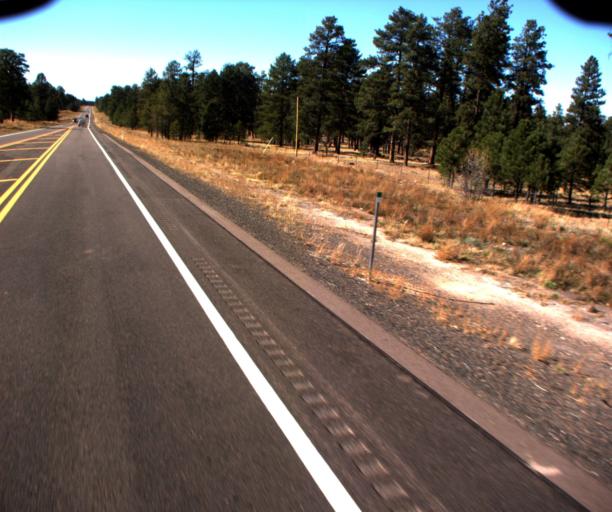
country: US
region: Arizona
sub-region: Apache County
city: Saint Michaels
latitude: 35.6817
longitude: -109.2191
